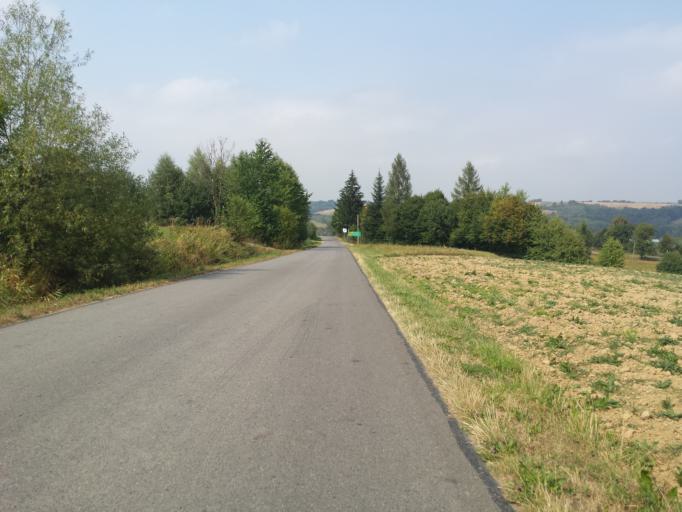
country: PL
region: Subcarpathian Voivodeship
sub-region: Powiat rzeszowski
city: Dynow
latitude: 49.8262
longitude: 22.2049
